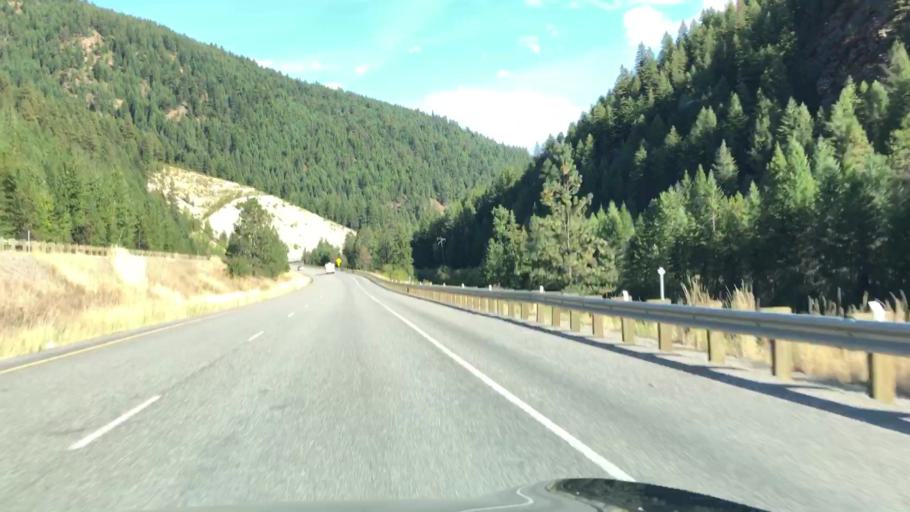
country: US
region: Montana
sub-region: Sanders County
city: Thompson Falls
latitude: 47.3130
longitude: -115.2188
